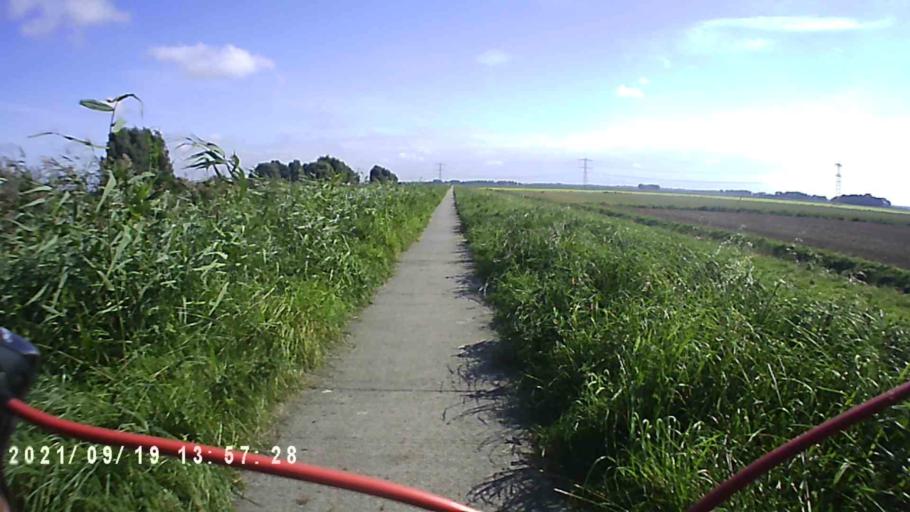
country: NL
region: Groningen
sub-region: Gemeente  Oldambt
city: Winschoten
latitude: 53.1435
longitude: 7.0892
